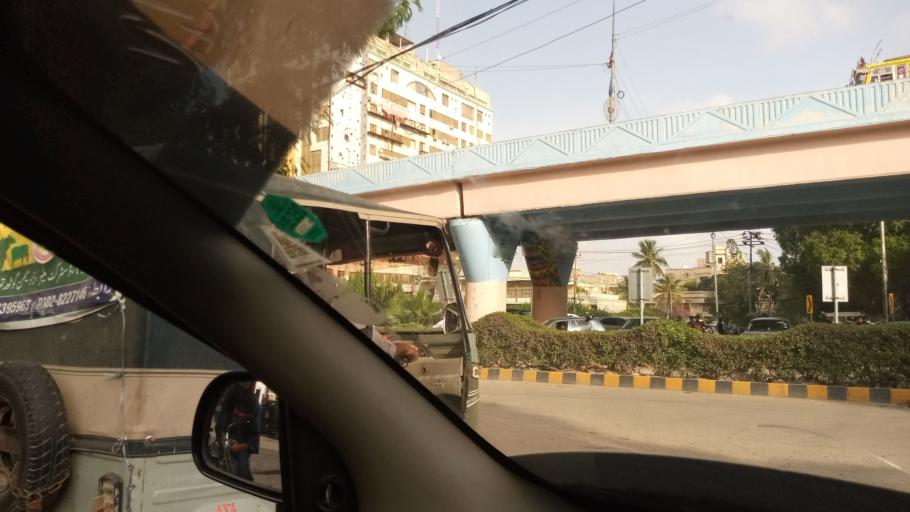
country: PK
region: Sindh
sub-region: Karachi District
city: Karachi
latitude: 24.8656
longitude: 67.0778
